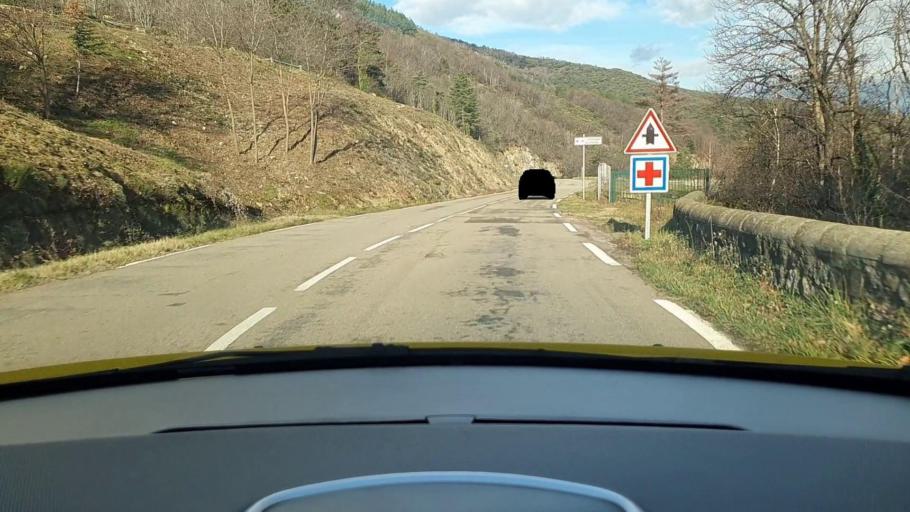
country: FR
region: Languedoc-Roussillon
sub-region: Departement du Gard
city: Branoux-les-Taillades
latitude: 44.3966
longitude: 3.9346
